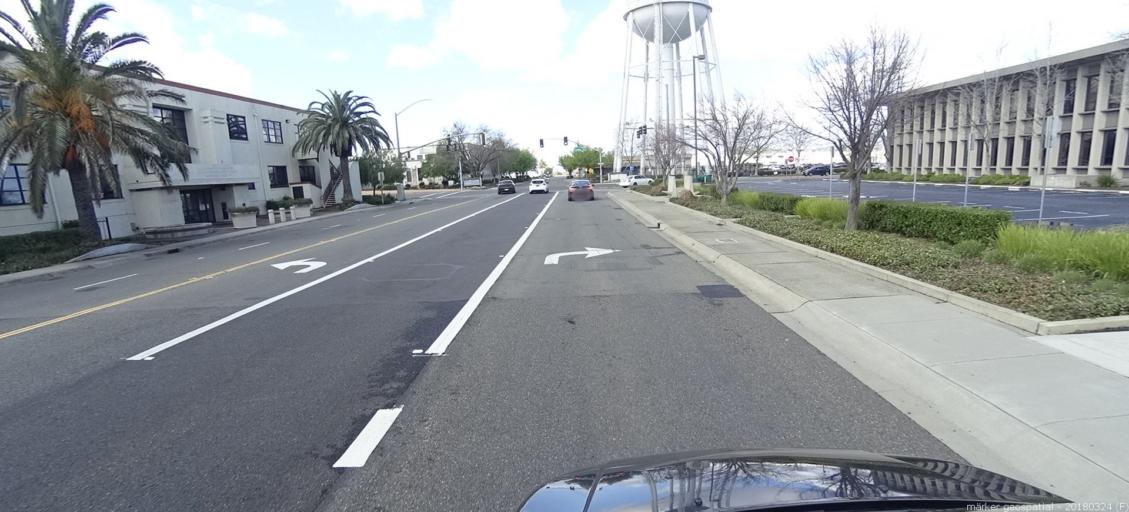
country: US
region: California
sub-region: Sacramento County
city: North Highlands
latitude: 38.6609
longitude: -121.3872
